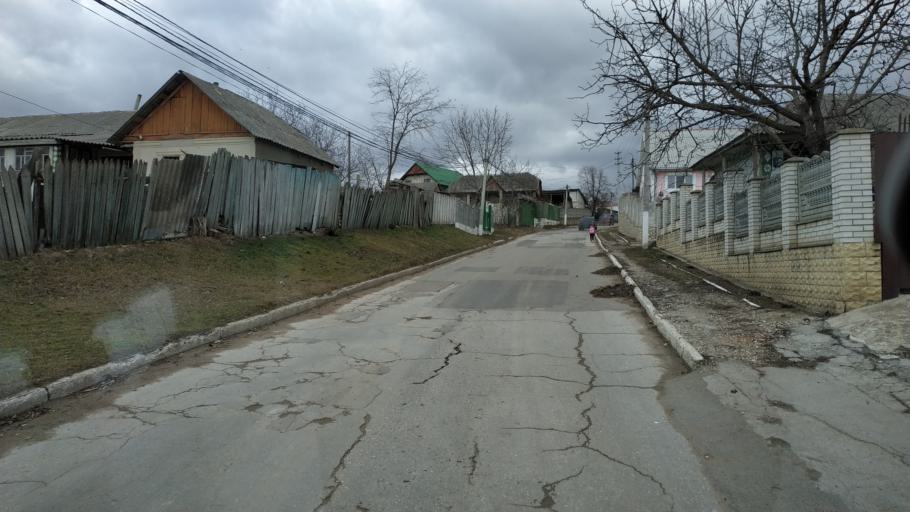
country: MD
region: Stinga Nistrului
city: Bucovat
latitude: 47.2317
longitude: 28.4245
